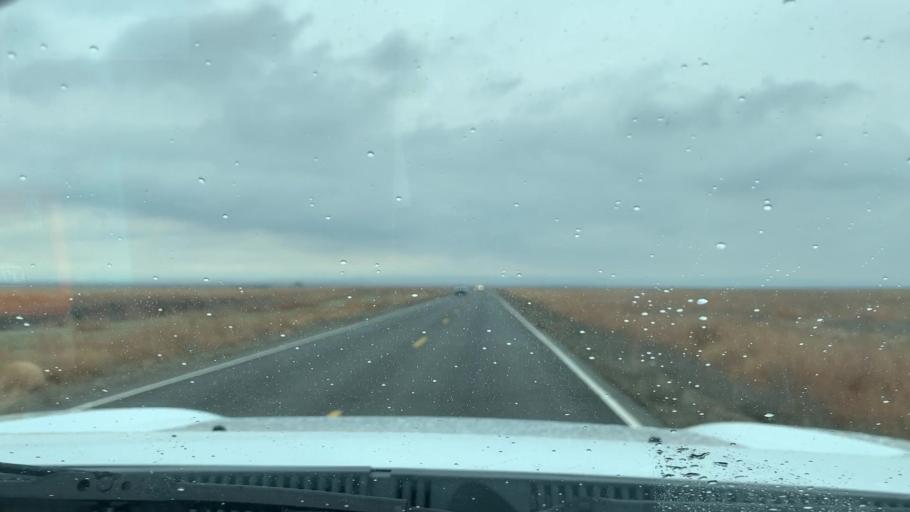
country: US
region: California
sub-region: Kings County
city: Kettleman City
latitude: 35.9340
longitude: -119.8107
